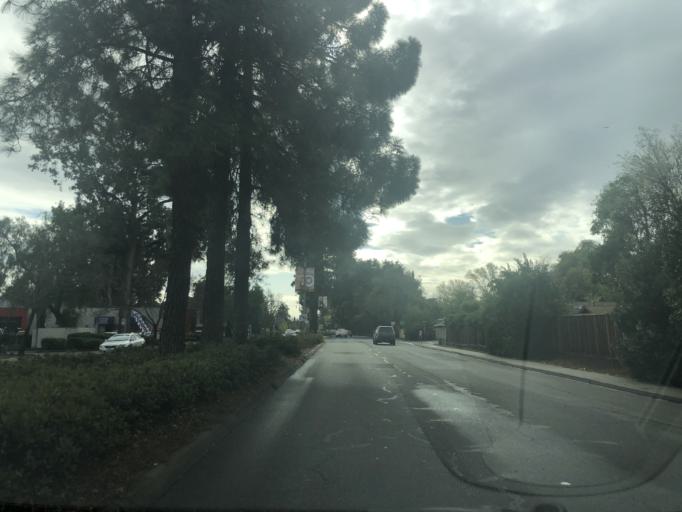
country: US
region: California
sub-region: Contra Costa County
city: Pleasant Hill
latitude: 37.9609
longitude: -122.0616
